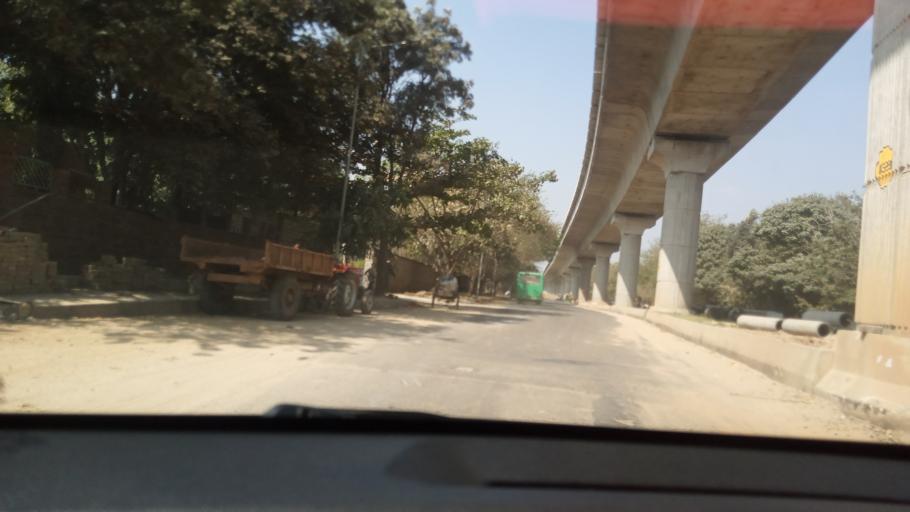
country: IN
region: Karnataka
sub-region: Bangalore Rural
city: Hoskote
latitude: 12.9767
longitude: 77.7232
